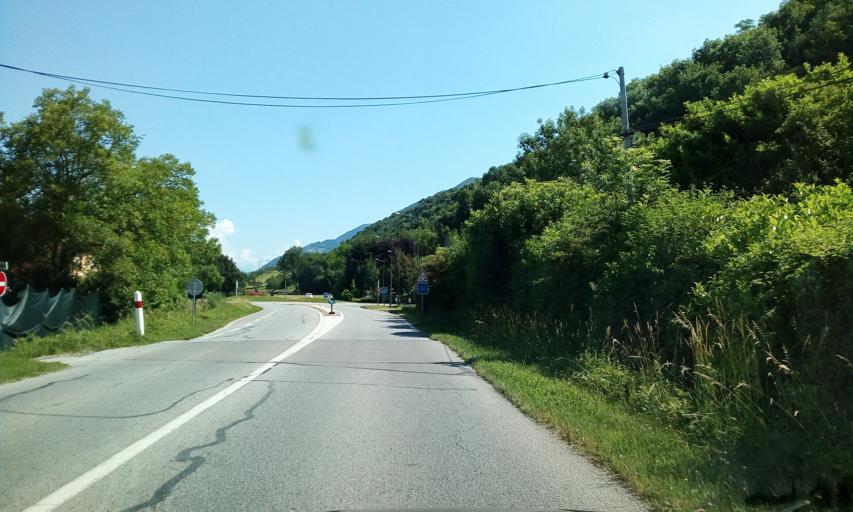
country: FR
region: Rhone-Alpes
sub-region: Departement de l'Isere
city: Tencin
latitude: 45.3140
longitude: 5.9633
